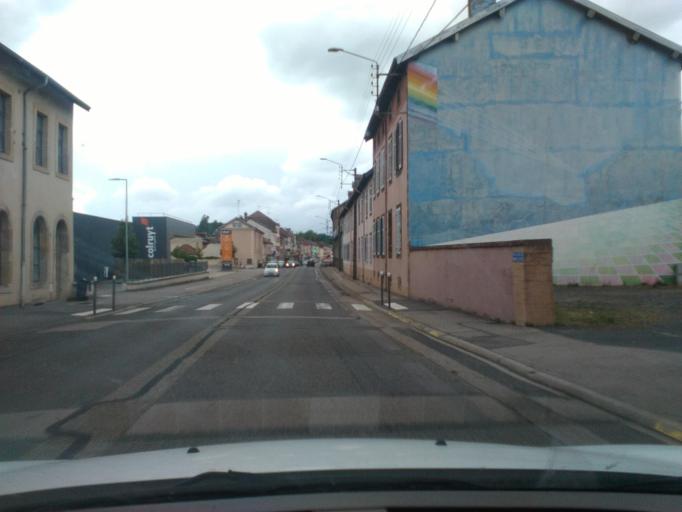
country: FR
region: Lorraine
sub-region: Departement de Meurthe-et-Moselle
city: Baccarat
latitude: 48.4471
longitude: 6.7437
